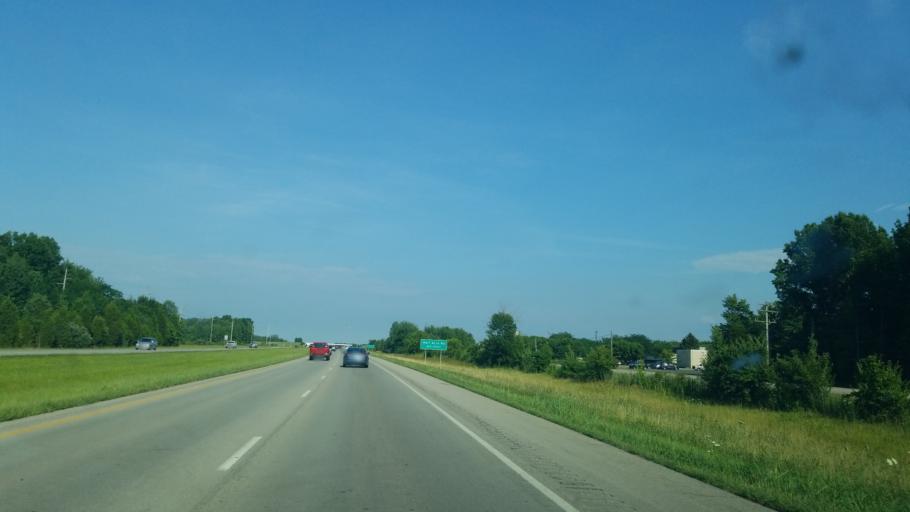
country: US
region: Ohio
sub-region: Clermont County
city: Williamsburg
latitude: 39.0715
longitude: -84.1039
